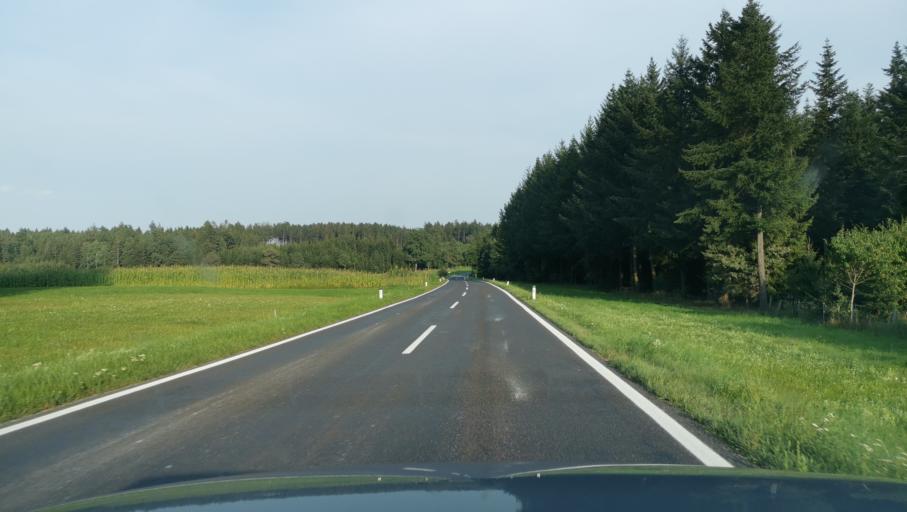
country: AT
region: Upper Austria
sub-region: Politischer Bezirk Grieskirchen
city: Grieskirchen
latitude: 48.3533
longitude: 13.7117
